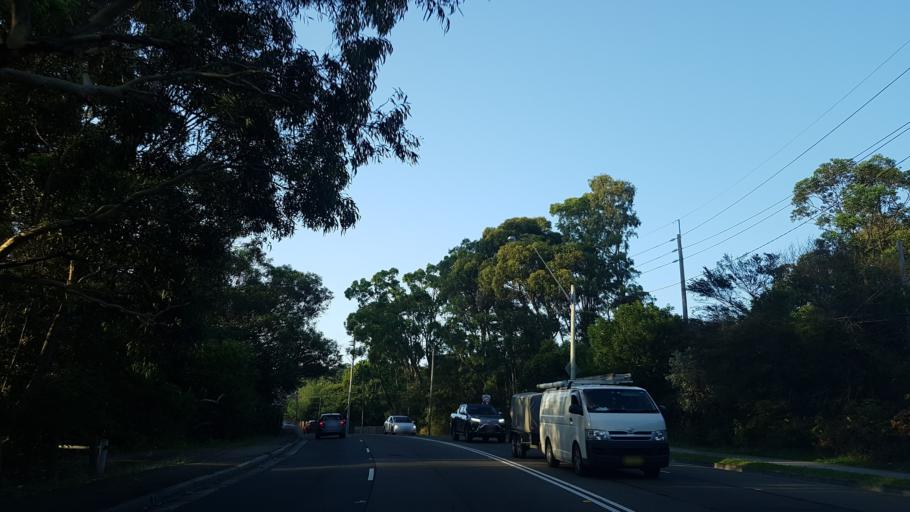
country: AU
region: New South Wales
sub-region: Warringah
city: Narraweena
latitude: -33.7480
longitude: 151.2623
